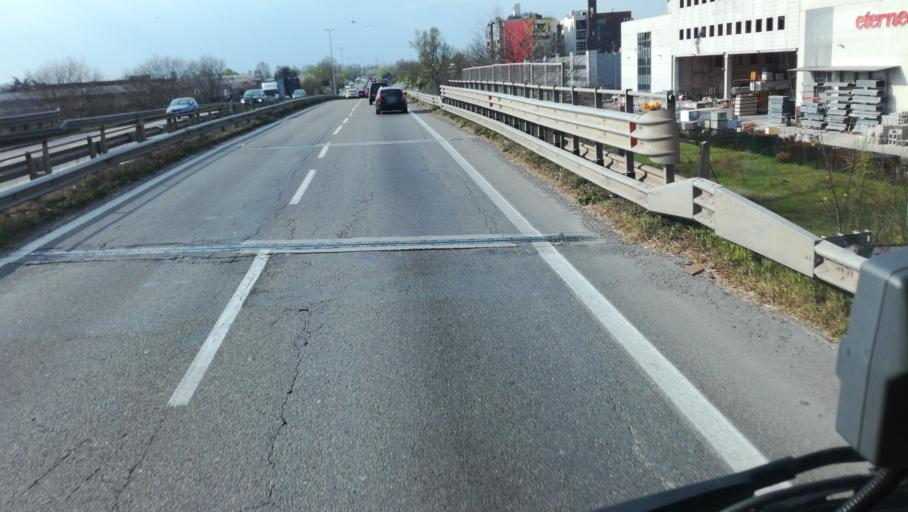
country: IT
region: Emilia-Romagna
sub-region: Provincia di Modena
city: Modena
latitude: 44.6633
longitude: 10.9413
